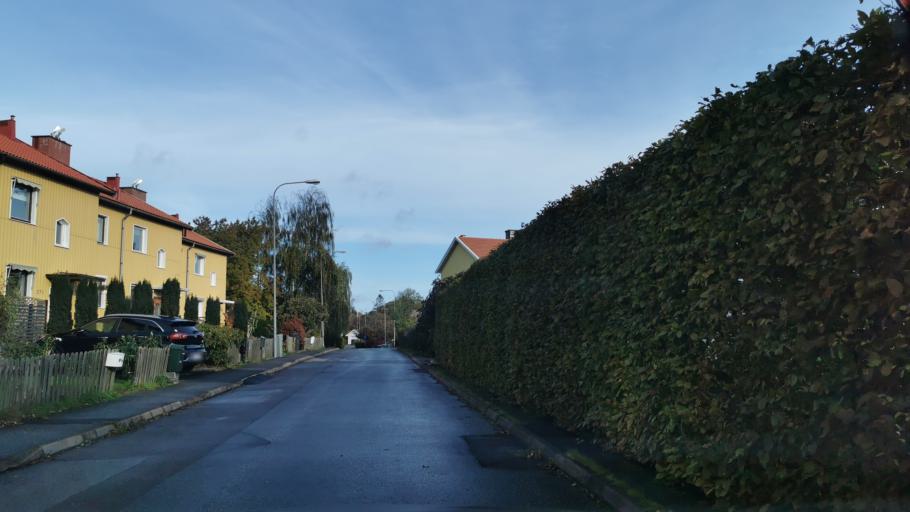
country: SE
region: Vaestra Goetaland
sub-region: Partille Kommun
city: Partille
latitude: 57.7299
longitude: 12.0869
